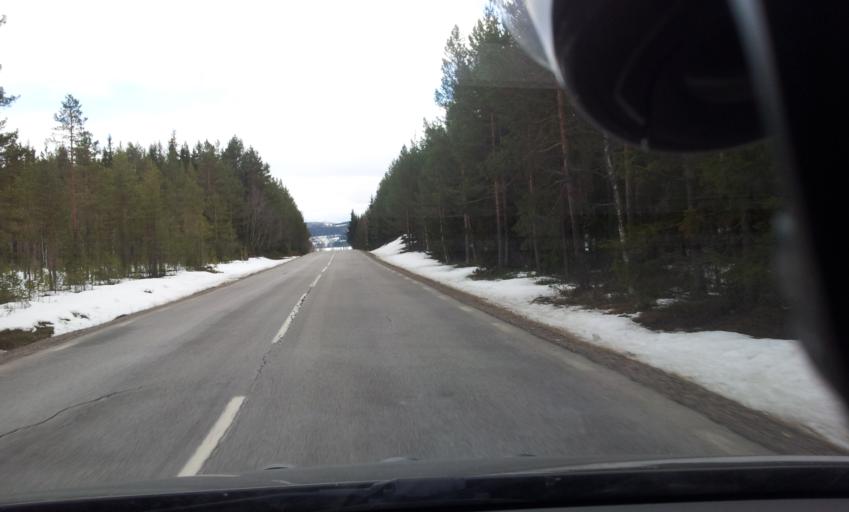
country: SE
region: Gaevleborg
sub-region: Ljusdals Kommun
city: Farila
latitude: 62.1421
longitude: 15.6871
